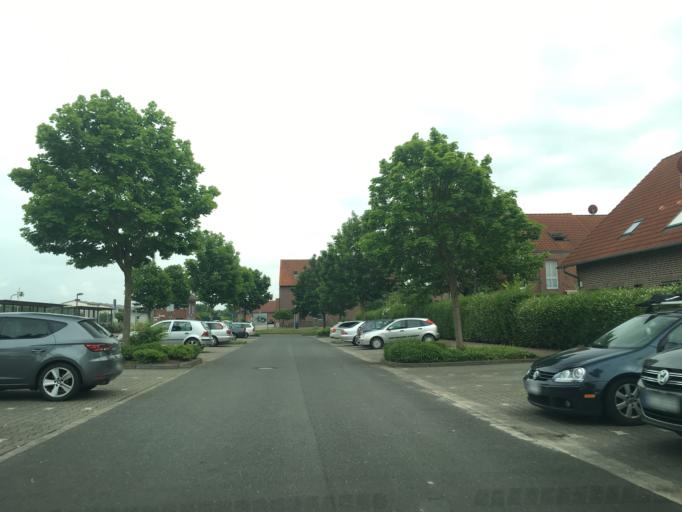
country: DE
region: North Rhine-Westphalia
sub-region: Regierungsbezirk Munster
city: Altenberge
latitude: 52.0515
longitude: 7.4814
